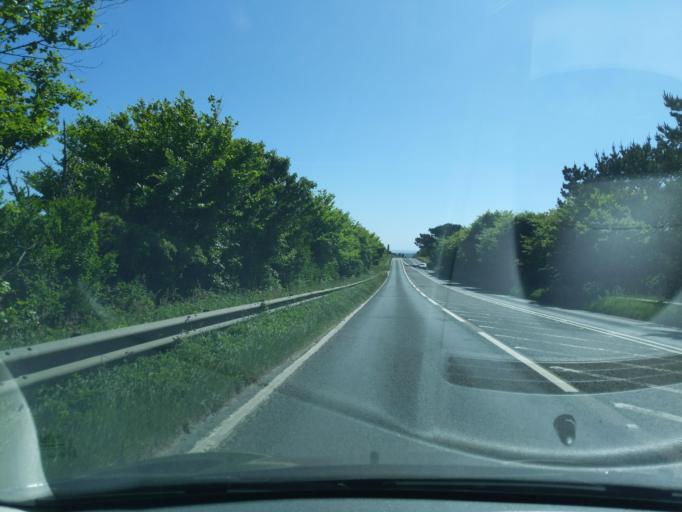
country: GB
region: England
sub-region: Cornwall
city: Wendron
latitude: 50.1332
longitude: -5.2242
